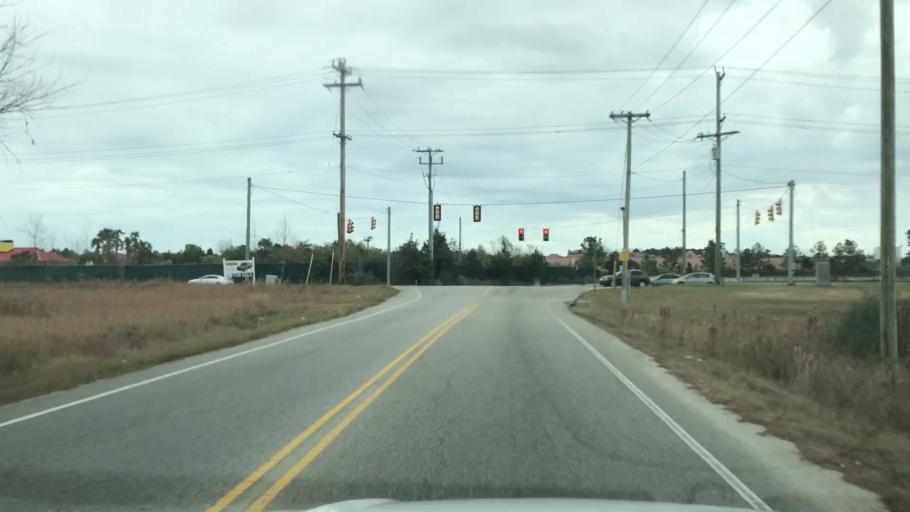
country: US
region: South Carolina
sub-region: Horry County
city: Forestbrook
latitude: 33.7149
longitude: -78.9378
